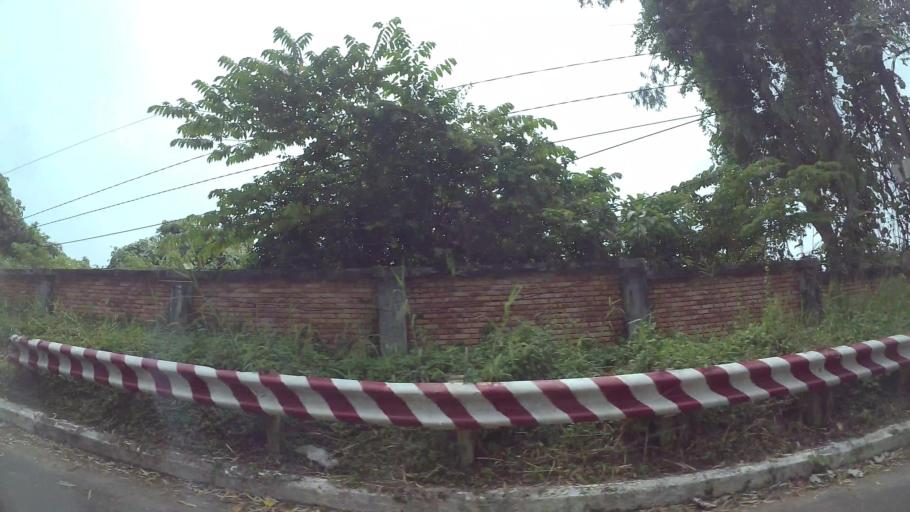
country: VN
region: Da Nang
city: Son Tra
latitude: 16.1064
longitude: 108.2992
